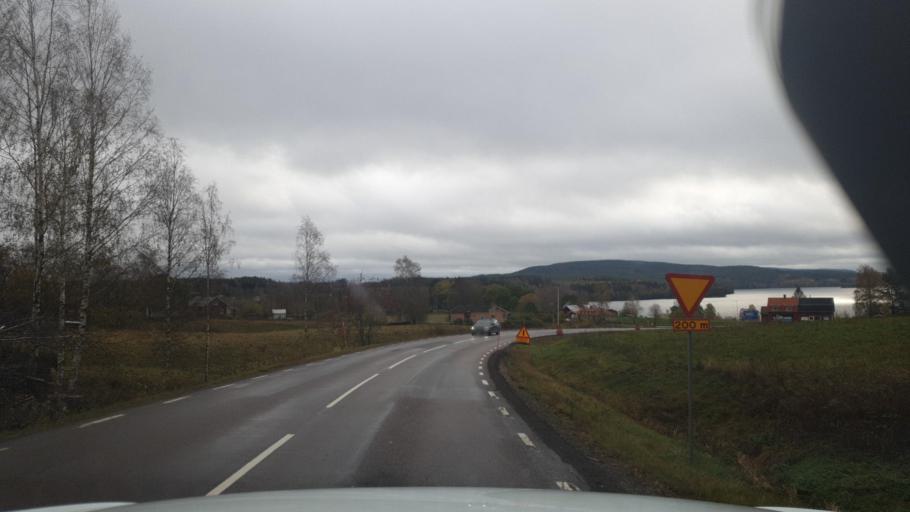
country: SE
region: Vaermland
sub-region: Eda Kommun
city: Amotfors
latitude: 59.7754
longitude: 12.2735
